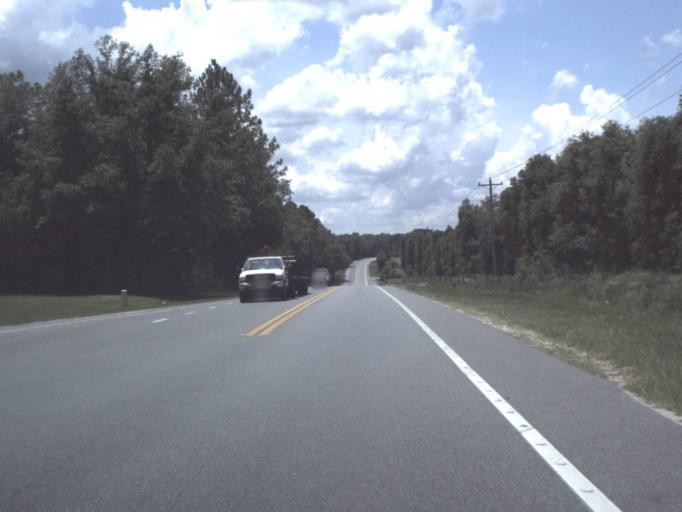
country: US
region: Florida
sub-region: Clay County
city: Keystone Heights
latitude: 29.7261
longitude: -81.9417
